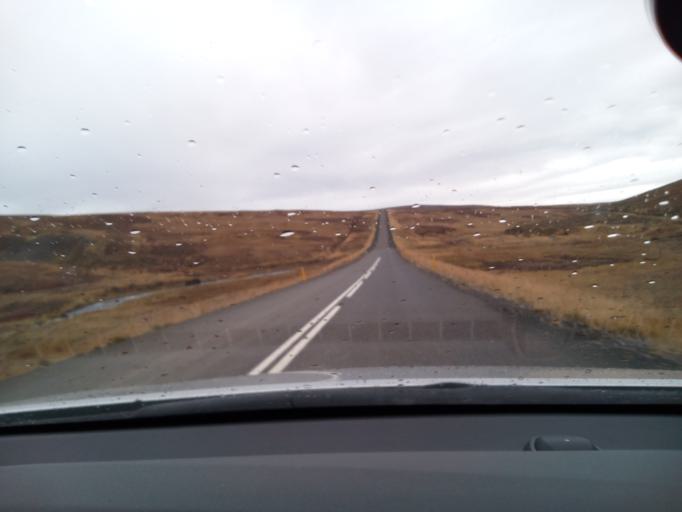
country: IS
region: Northeast
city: Laugar
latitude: 65.7930
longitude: -17.2353
